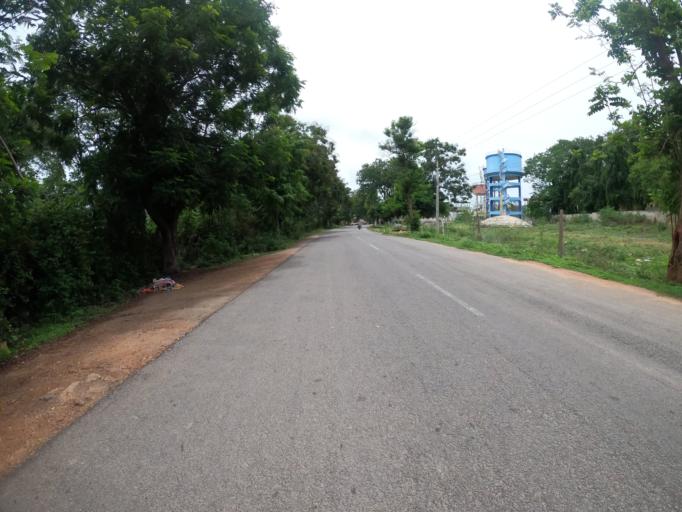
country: IN
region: Telangana
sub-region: Hyderabad
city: Hyderabad
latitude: 17.3405
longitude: 78.3611
